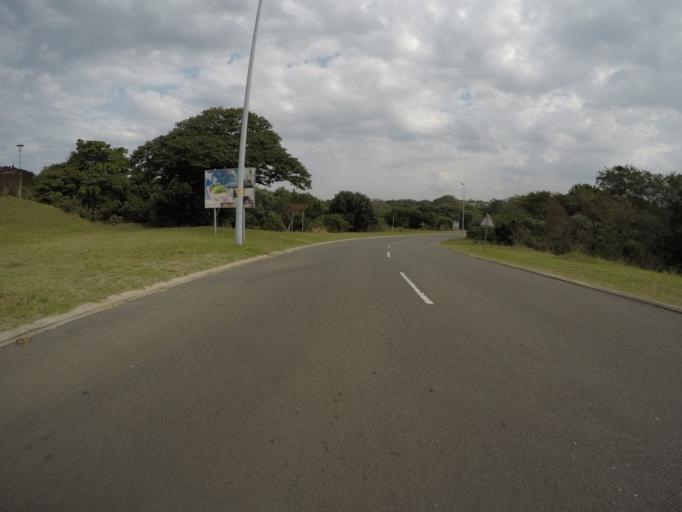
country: ZA
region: KwaZulu-Natal
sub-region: uThungulu District Municipality
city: Richards Bay
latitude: -28.7373
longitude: 32.0928
